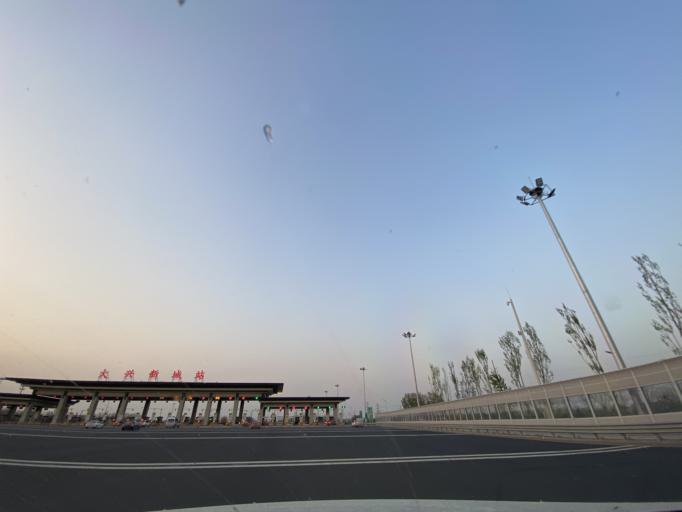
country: CN
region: Beijing
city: Xingfeng
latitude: 39.7268
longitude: 116.3792
